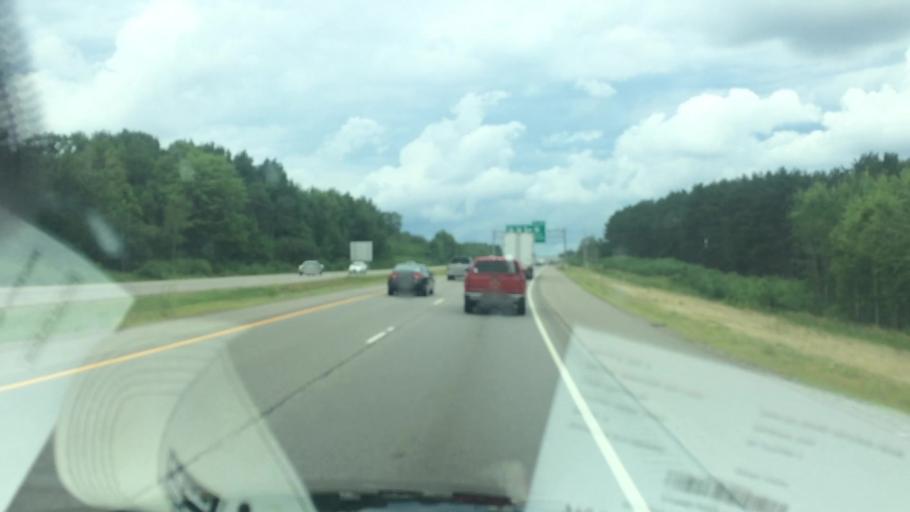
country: US
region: Wisconsin
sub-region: Marathon County
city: Rothschild
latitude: 44.8730
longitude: -89.6450
